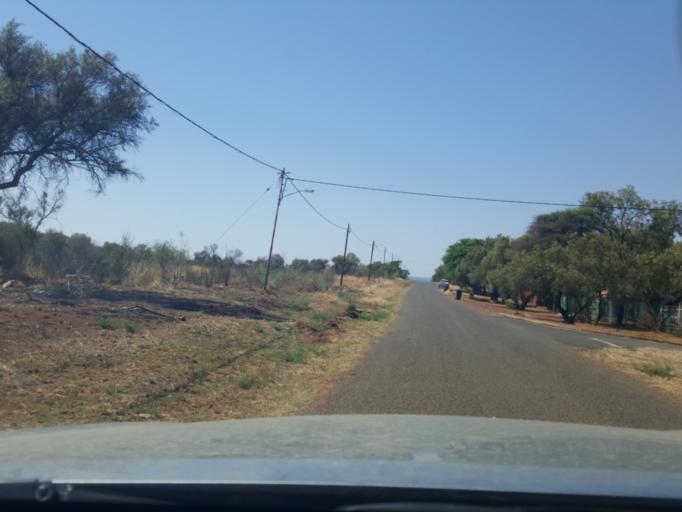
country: ZA
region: North-West
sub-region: Ngaka Modiri Molema District Municipality
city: Zeerust
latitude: -25.5287
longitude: 26.0807
